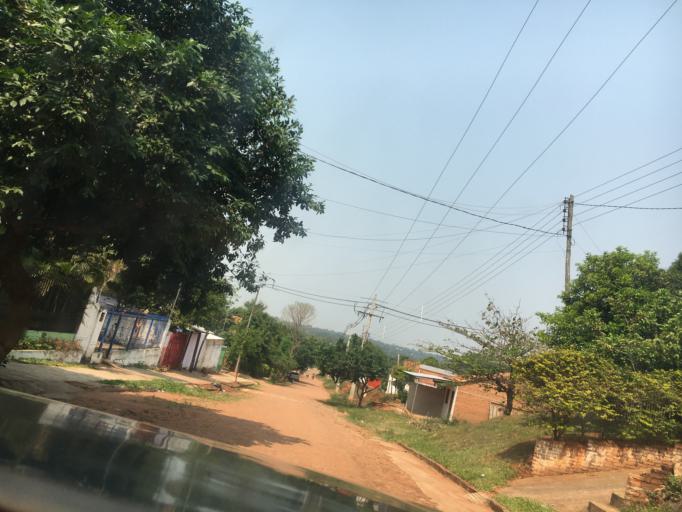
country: PY
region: Central
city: Nemby
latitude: -25.3895
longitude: -57.5645
